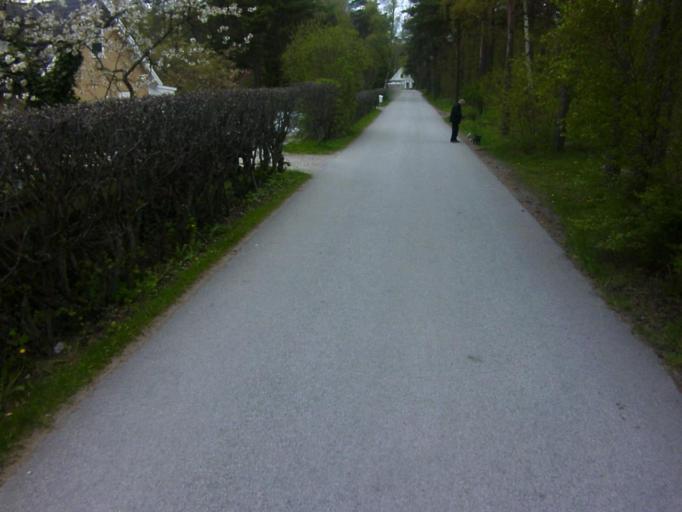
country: SE
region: Skane
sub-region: Kavlinge Kommun
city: Loddekopinge
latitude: 55.7544
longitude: 12.9946
